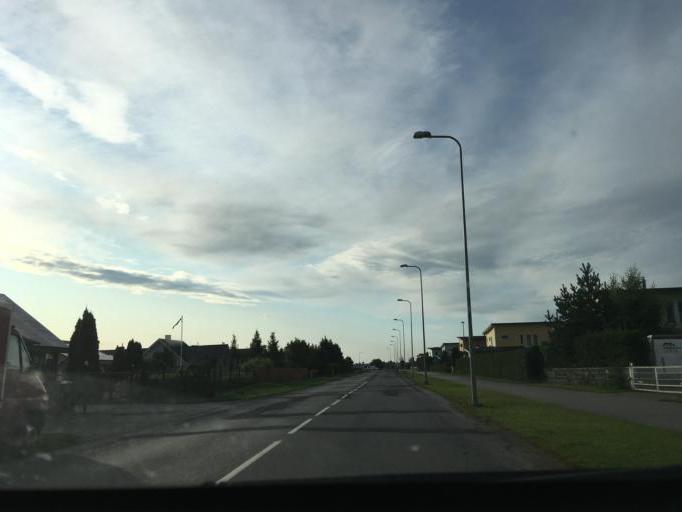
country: EE
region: Harju
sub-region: Tallinna linn
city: Tallinn
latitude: 59.3946
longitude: 24.8146
